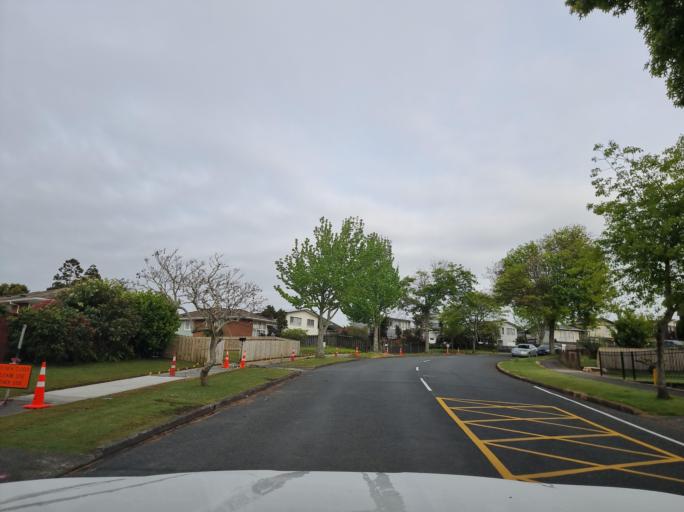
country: NZ
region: Northland
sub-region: Whangarei
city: Whangarei
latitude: -35.7515
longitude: 174.3616
